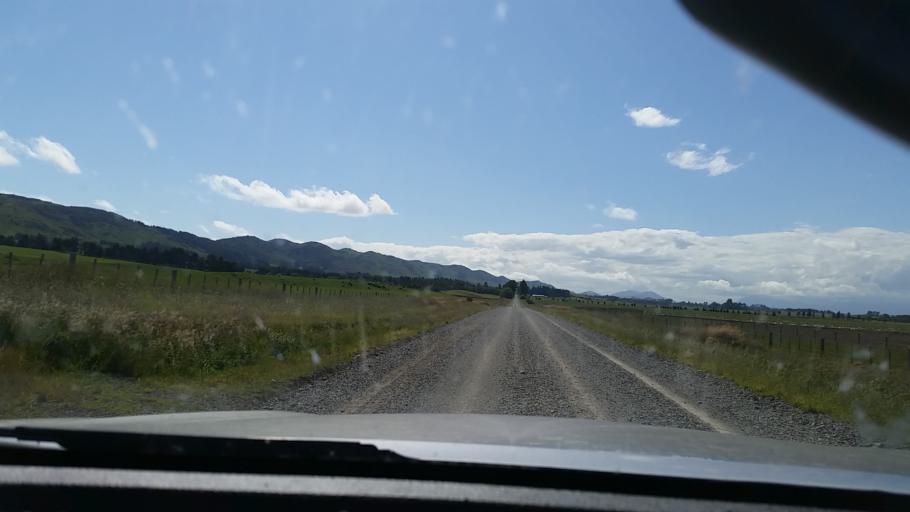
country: NZ
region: Southland
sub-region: Southland District
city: Winton
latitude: -45.8958
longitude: 168.5405
